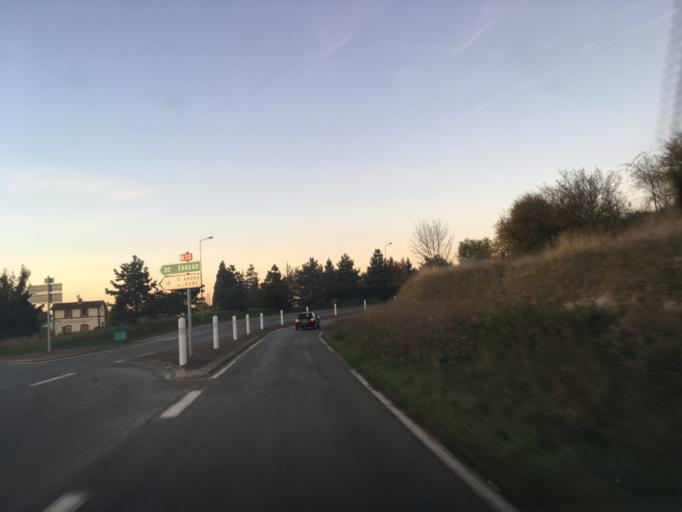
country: FR
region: Haute-Normandie
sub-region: Departement de l'Eure
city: Pacy-sur-Eure
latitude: 49.0088
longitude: 1.3907
